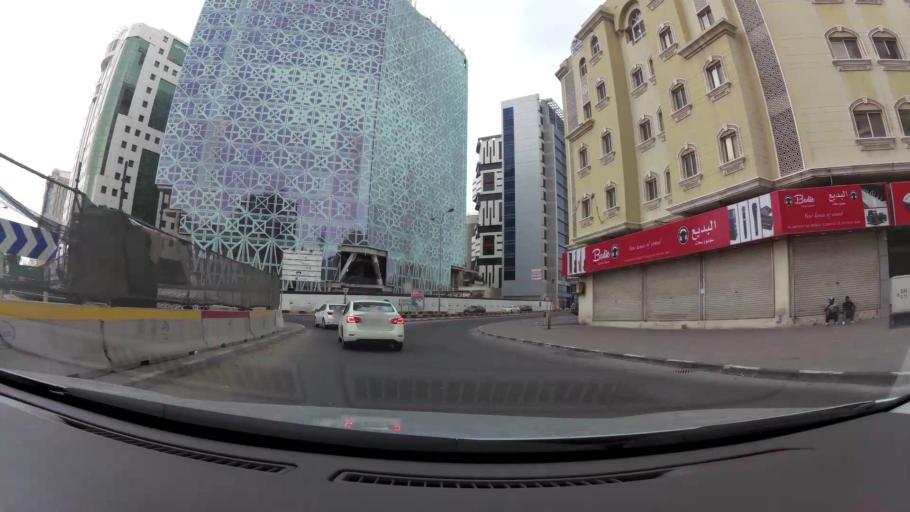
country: QA
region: Baladiyat ad Dawhah
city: Doha
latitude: 25.2864
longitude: 51.5400
